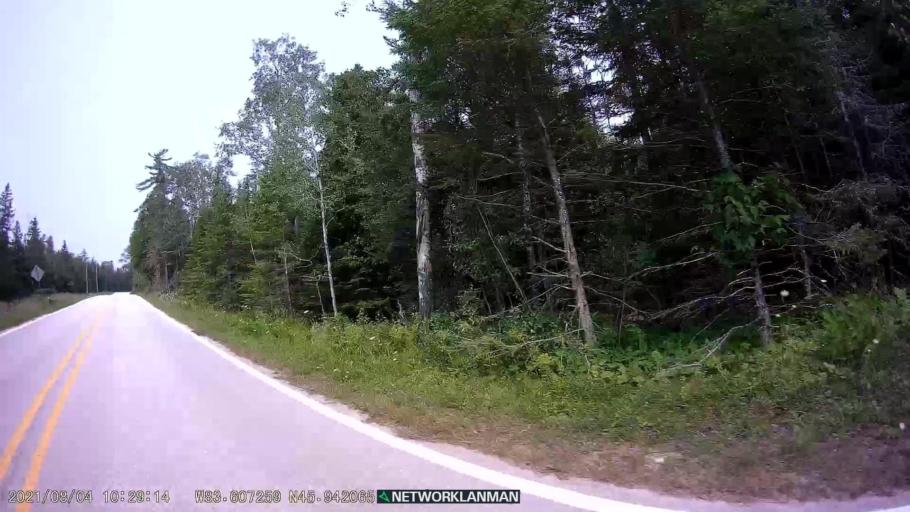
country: CA
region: Ontario
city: Thessalon
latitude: 45.9422
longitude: -83.6075
